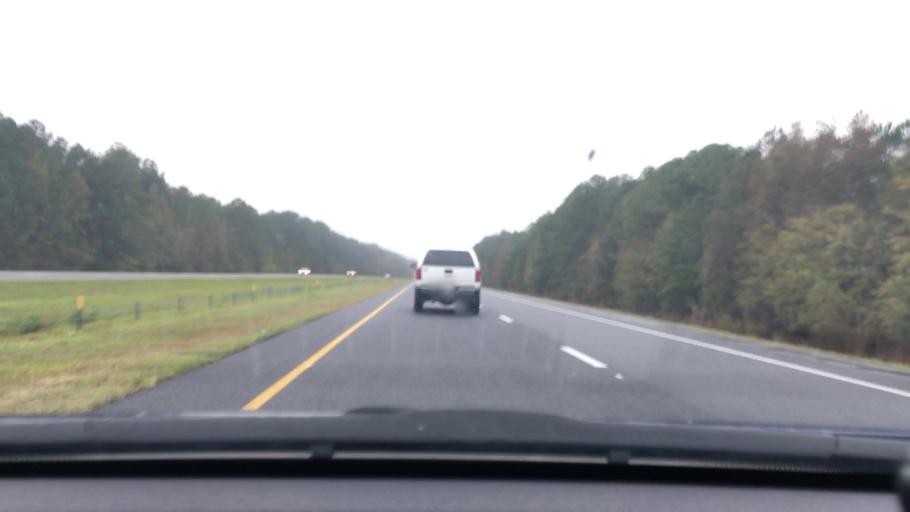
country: US
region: South Carolina
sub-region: Lee County
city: Bishopville
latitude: 34.1961
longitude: -80.1162
